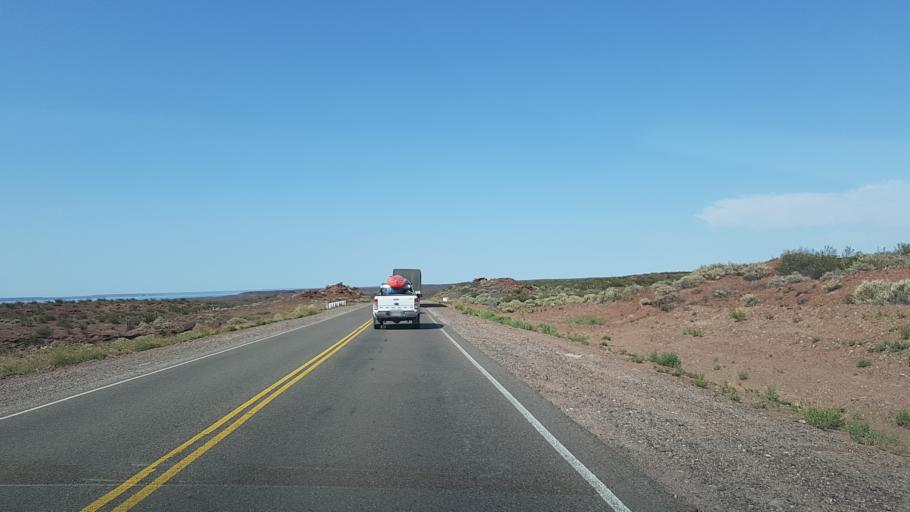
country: AR
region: Neuquen
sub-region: Departamento de Picun Leufu
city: Picun Leufu
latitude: -39.2758
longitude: -68.8558
